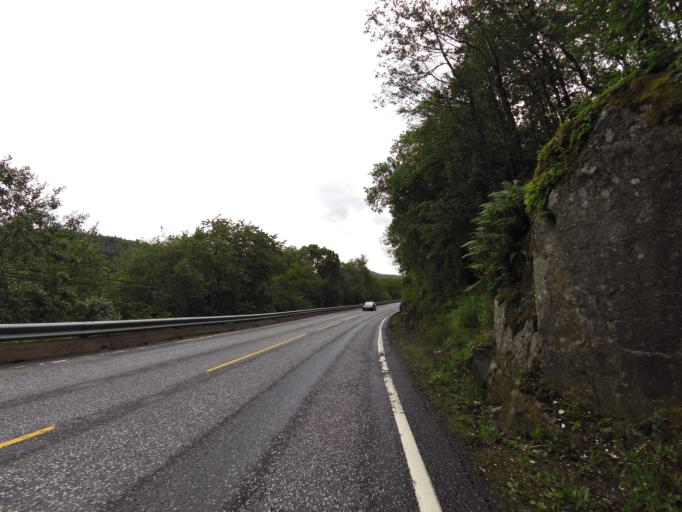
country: NO
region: Vest-Agder
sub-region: Farsund
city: Farsund
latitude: 58.1049
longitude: 6.9094
